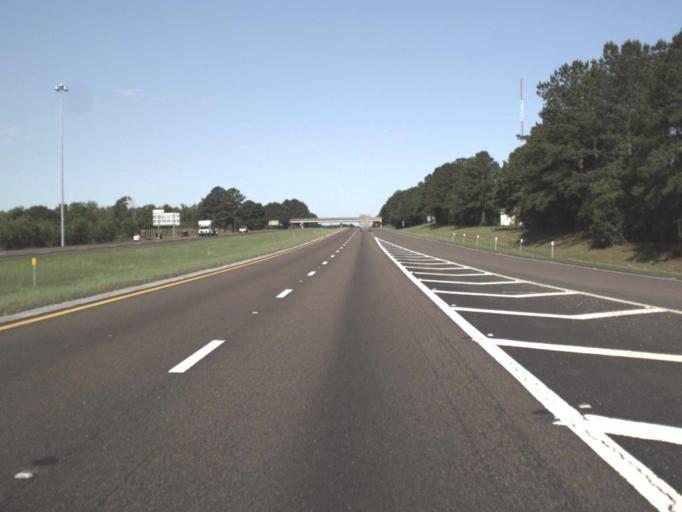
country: US
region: Florida
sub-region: Holmes County
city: Bonifay
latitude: 30.7630
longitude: -85.6890
